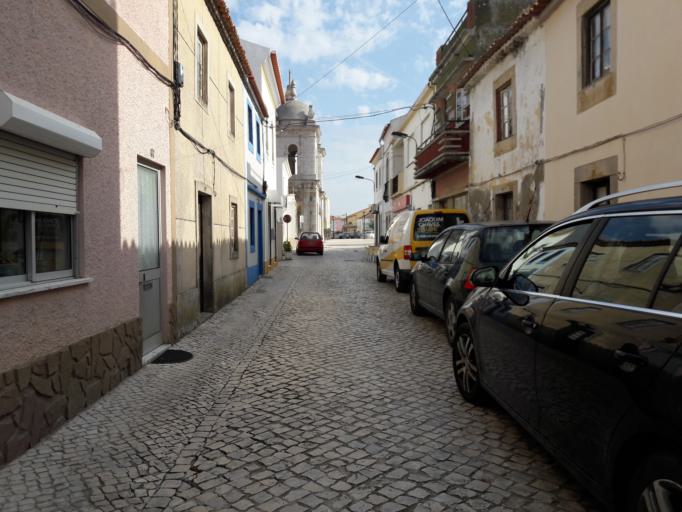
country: PT
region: Leiria
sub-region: Peniche
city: Atouguia da Baleia
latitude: 39.3372
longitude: -9.3255
